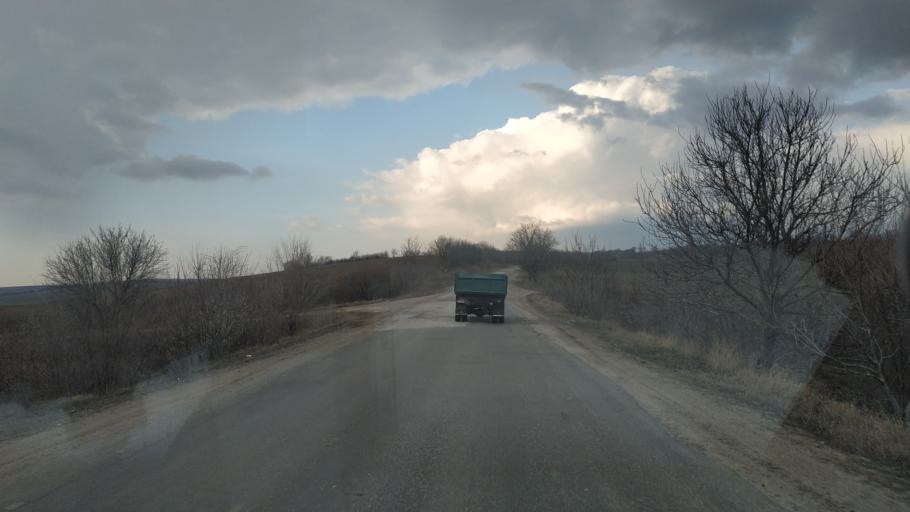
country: MD
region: Anenii Noi
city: Anenii Noi
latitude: 46.9486
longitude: 29.2826
